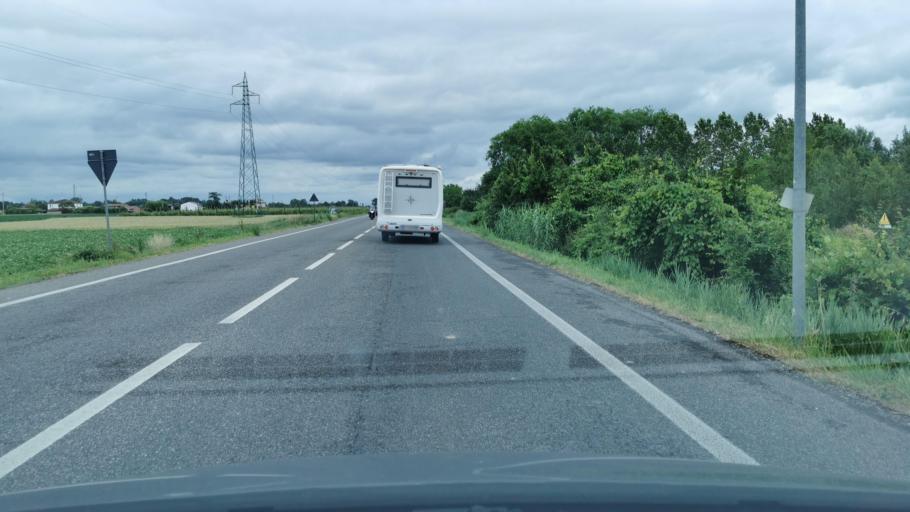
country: IT
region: Emilia-Romagna
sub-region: Provincia di Ravenna
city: Granarolo
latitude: 44.3628
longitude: 11.9342
